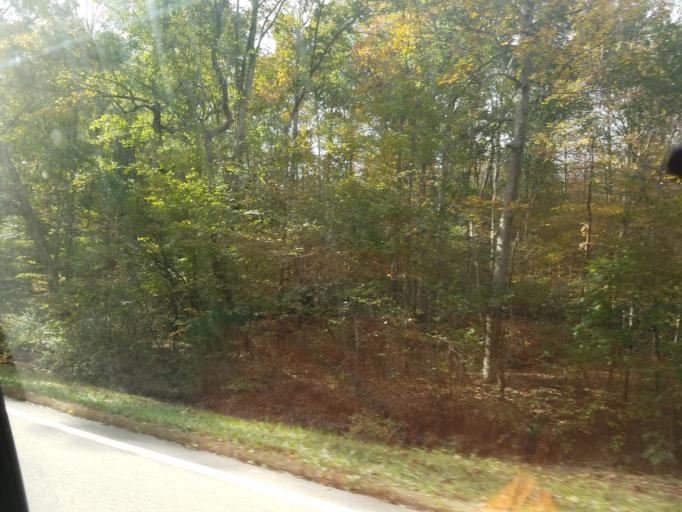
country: US
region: Ohio
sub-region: Vinton County
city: McArthur
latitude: 39.1646
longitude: -82.4362
